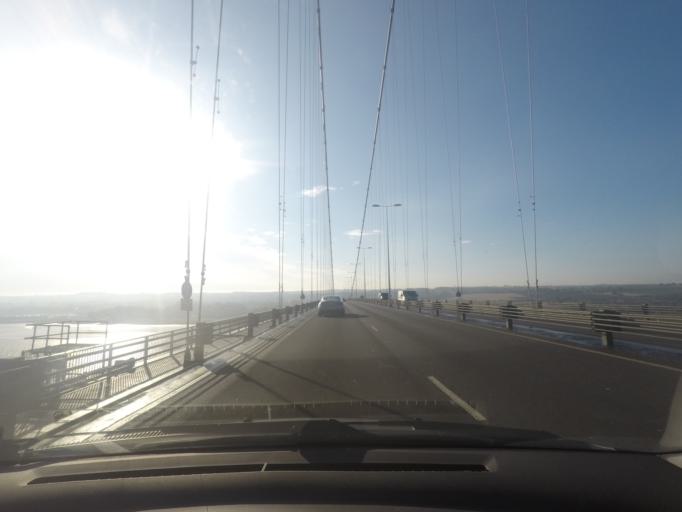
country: GB
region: England
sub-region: North Lincolnshire
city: Barton upon Humber
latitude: 53.7015
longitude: -0.4493
